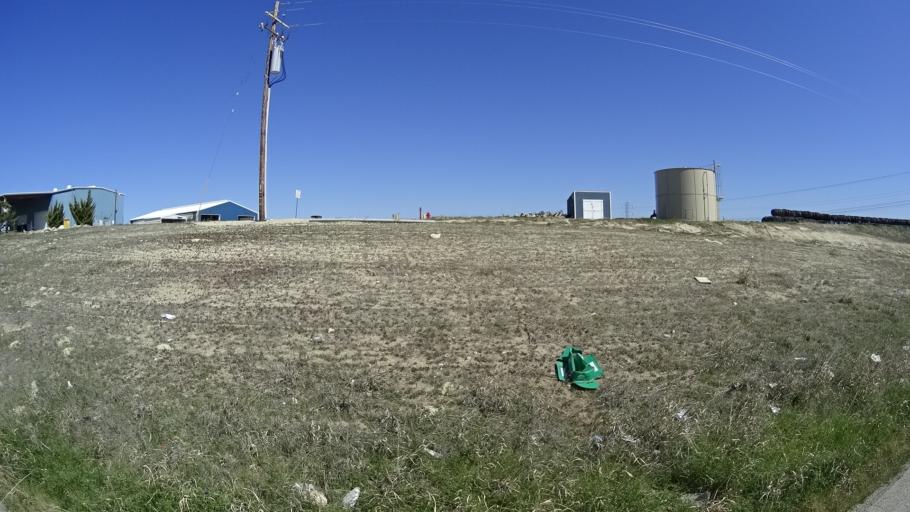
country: US
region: California
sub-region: Glenn County
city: Willows
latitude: 39.6313
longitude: -122.2758
